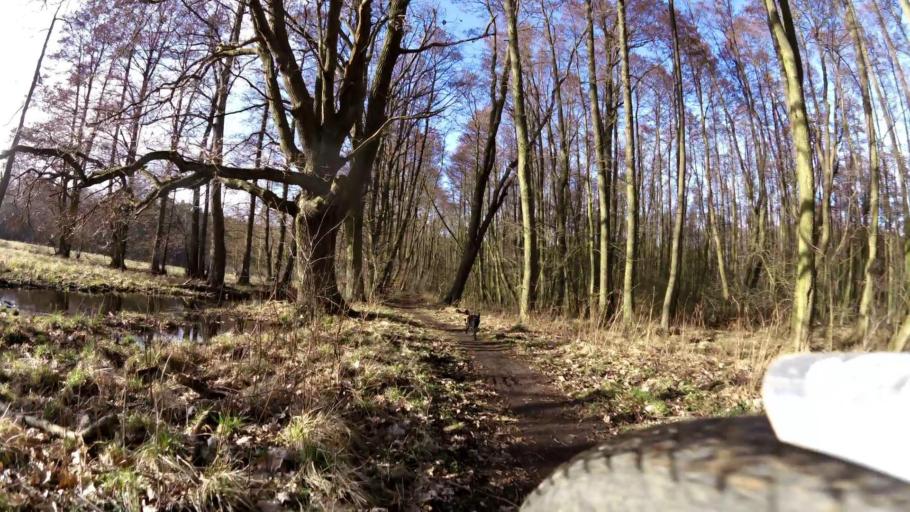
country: PL
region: West Pomeranian Voivodeship
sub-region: Powiat kamienski
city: Wolin
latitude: 53.8470
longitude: 14.7063
